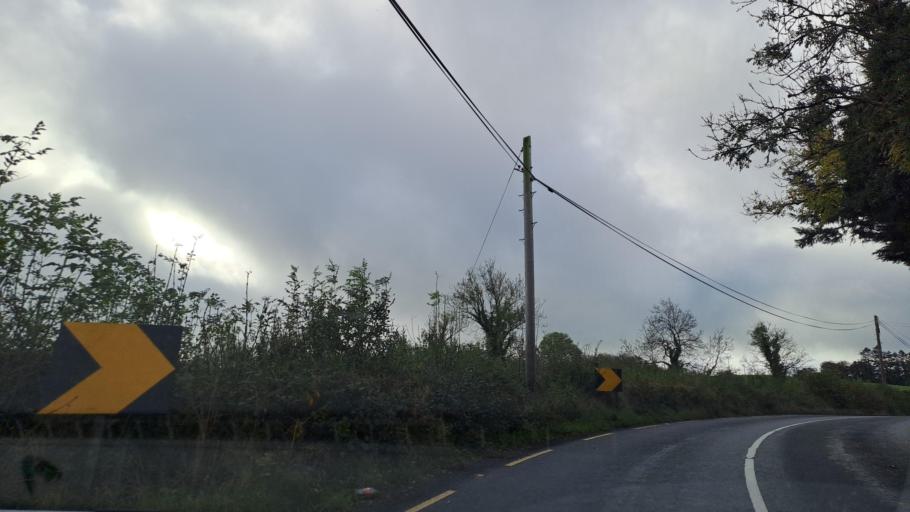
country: IE
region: Ulster
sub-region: An Cabhan
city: Virginia
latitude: 53.8655
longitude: -7.0423
